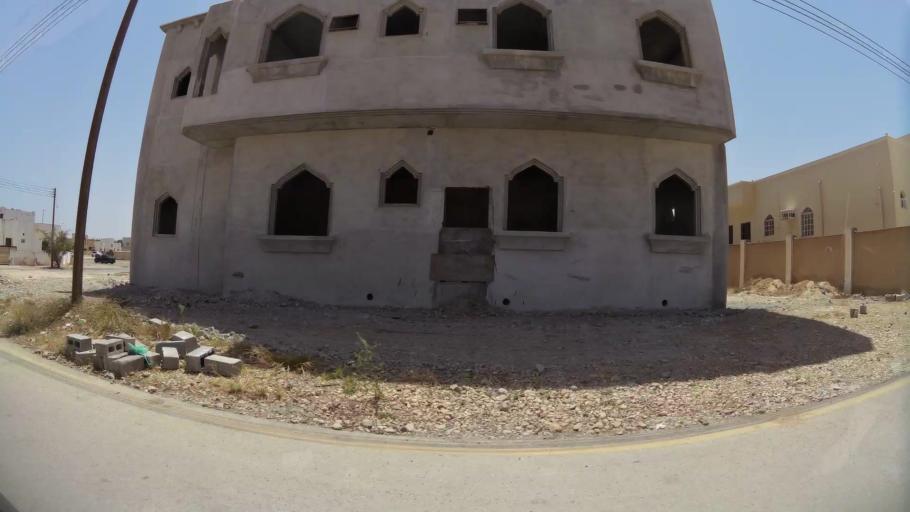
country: OM
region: Zufar
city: Salalah
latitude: 17.0649
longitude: 54.1562
